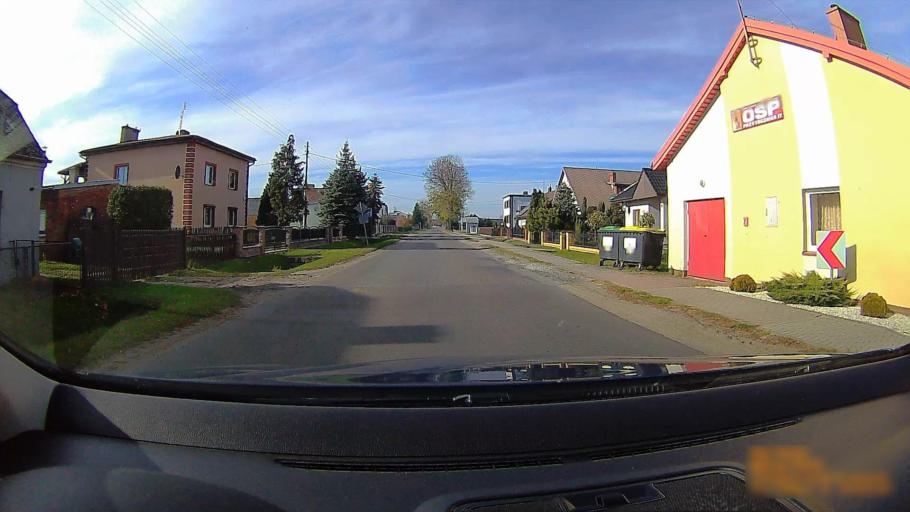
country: PL
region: Greater Poland Voivodeship
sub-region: Powiat ostrzeszowski
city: Doruchow
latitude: 51.4279
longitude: 18.0506
